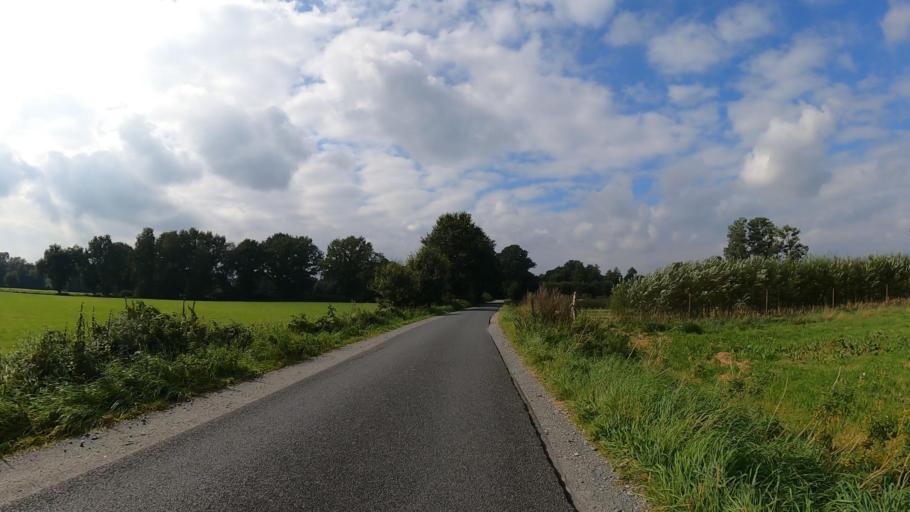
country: DE
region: Schleswig-Holstein
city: Kolln-Reisiek
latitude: 53.7250
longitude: 9.6906
